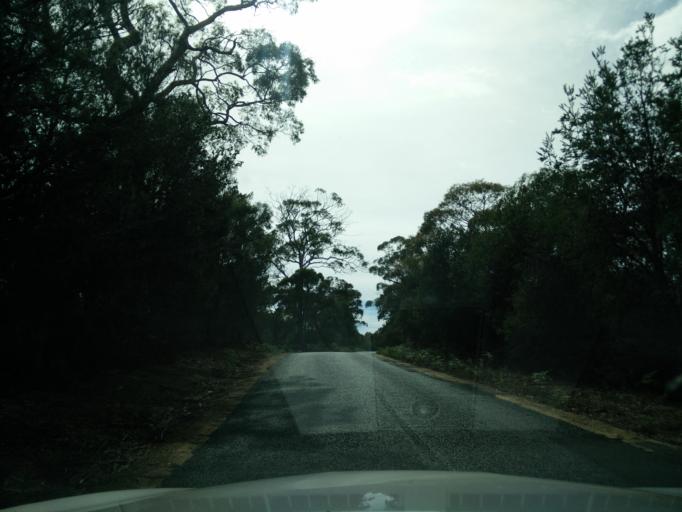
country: AU
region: Tasmania
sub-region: Break O'Day
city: St Helens
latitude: -42.0005
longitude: 148.2498
